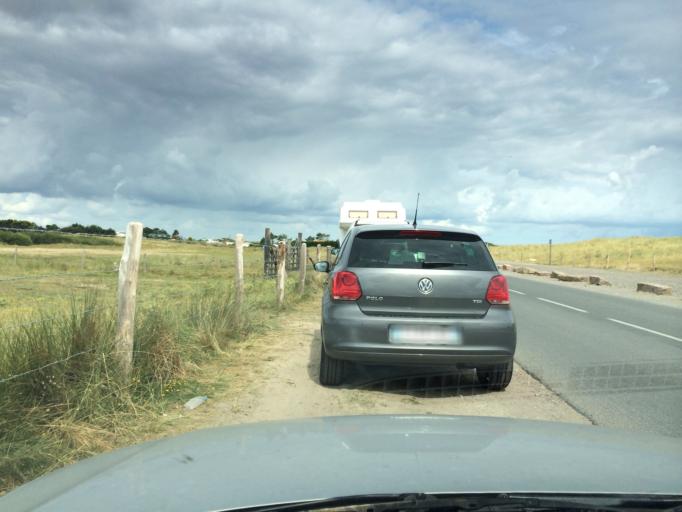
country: FR
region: Lower Normandy
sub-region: Departement de la Manche
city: Saint-Hilaire-Petitville
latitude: 49.4168
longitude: -1.1770
